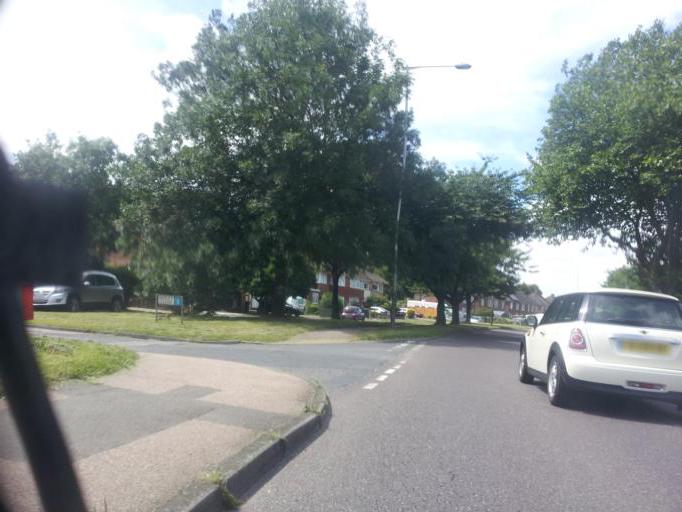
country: GB
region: England
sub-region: Kent
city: Aylesford
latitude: 51.3005
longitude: 0.4736
